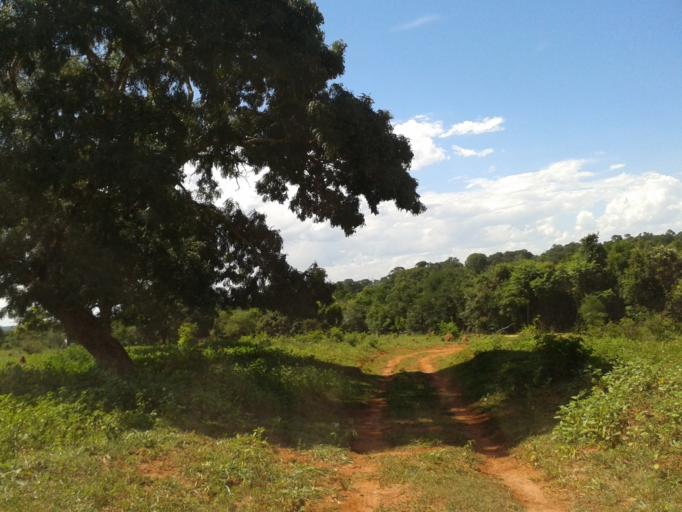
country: BR
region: Minas Gerais
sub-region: Santa Vitoria
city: Santa Vitoria
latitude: -19.1490
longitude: -50.5335
